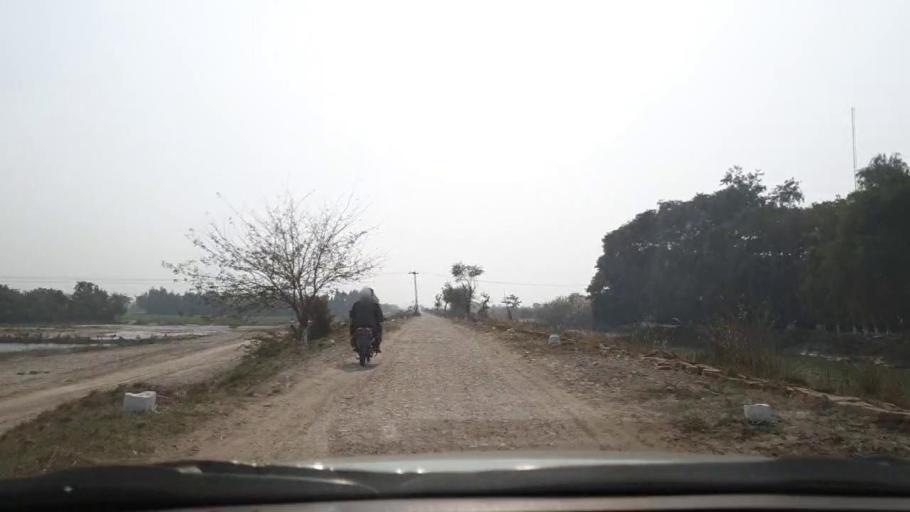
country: PK
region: Sindh
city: Matiari
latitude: 25.6432
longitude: 68.5606
